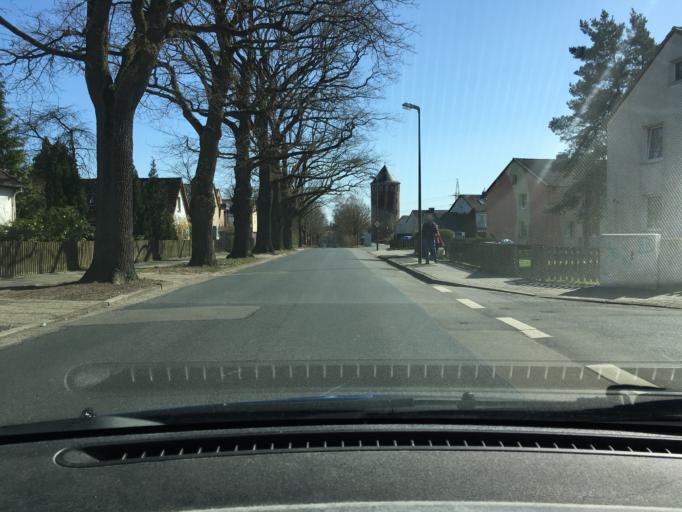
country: DE
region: Lower Saxony
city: Uelzen
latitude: 52.9641
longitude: 10.5376
